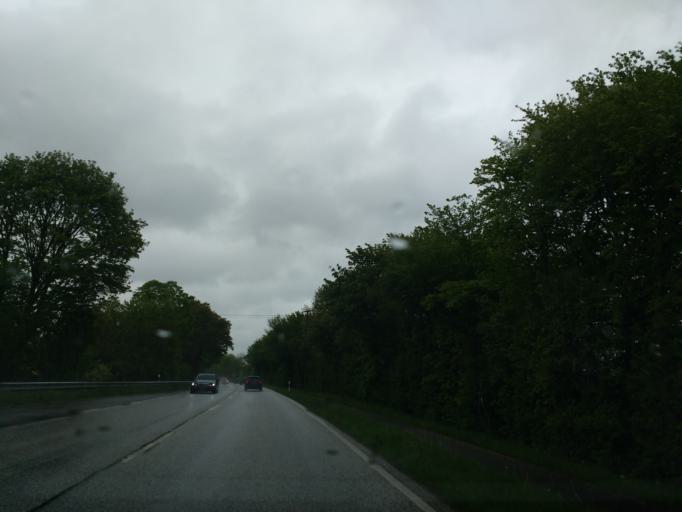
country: DE
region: Schleswig-Holstein
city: Barkelsby
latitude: 54.4945
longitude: 9.8404
